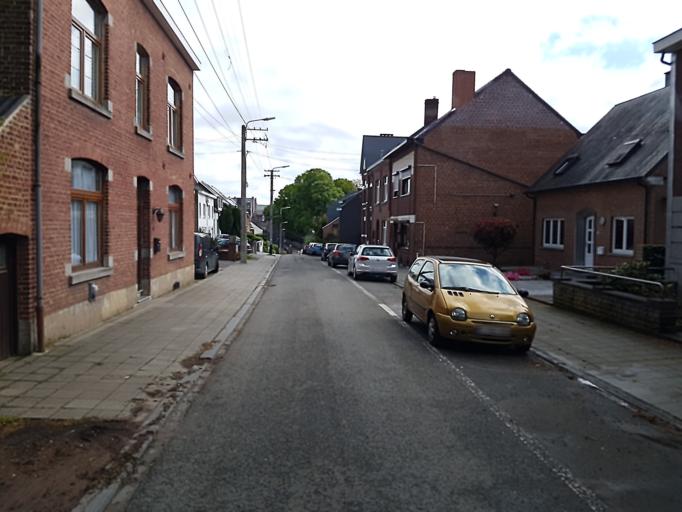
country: BE
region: Wallonia
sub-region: Province de Namur
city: Gembloux
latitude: 50.5647
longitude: 4.6910
